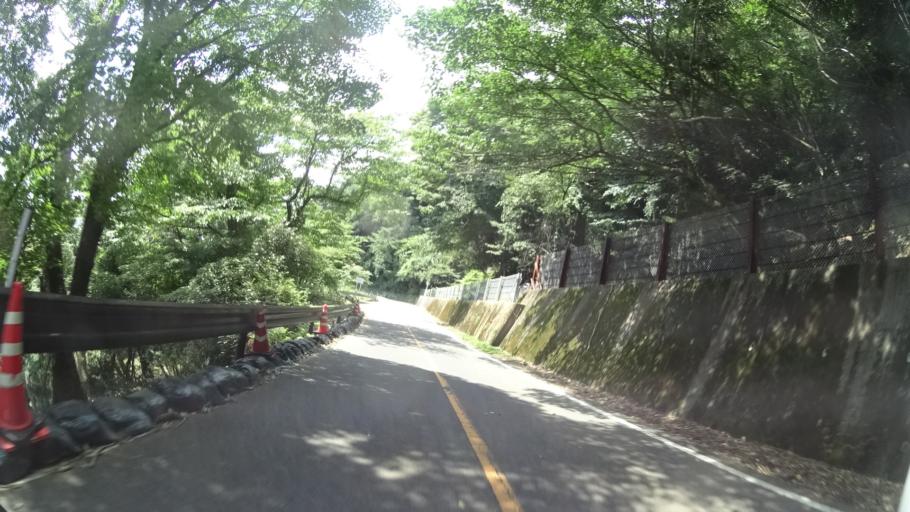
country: JP
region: Miyazaki
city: Kobayashi
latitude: 31.9015
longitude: 130.8416
